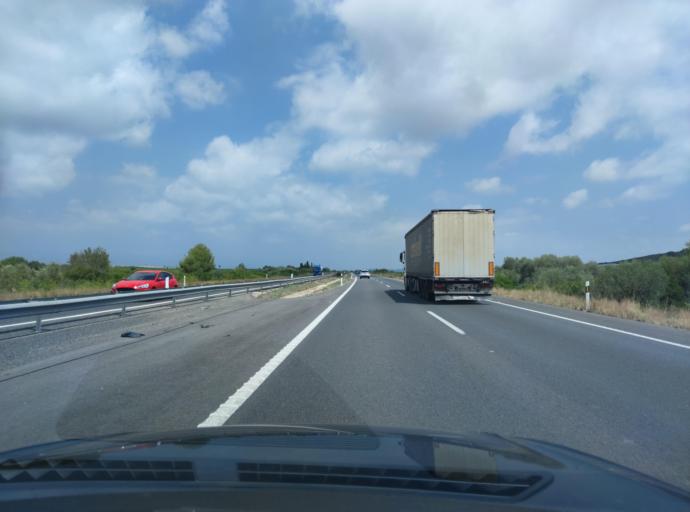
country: ES
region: Valencia
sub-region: Provincia de Castello
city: Vinaros
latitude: 40.5039
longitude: 0.4159
